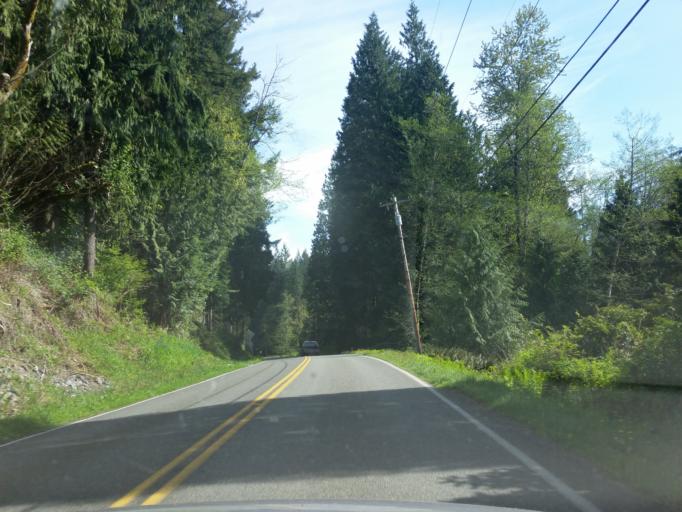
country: US
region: Washington
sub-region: Snohomish County
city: Three Lakes
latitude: 47.9850
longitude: -121.9175
